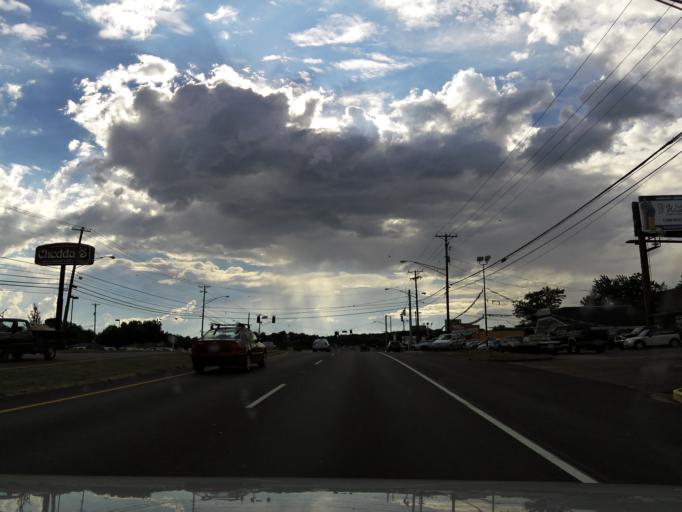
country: US
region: Tennessee
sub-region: Knox County
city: Knoxville
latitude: 36.0055
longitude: -83.9853
